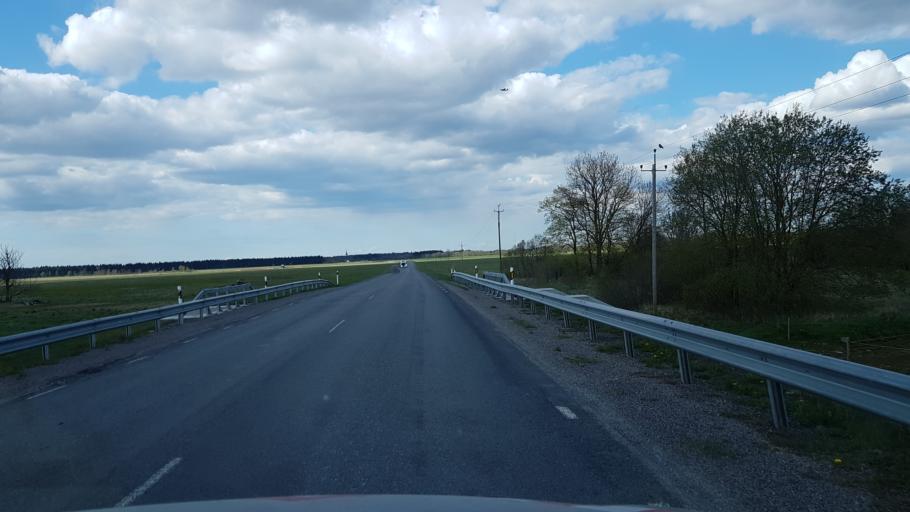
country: EE
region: Harju
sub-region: Keila linn
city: Keila
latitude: 59.2775
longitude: 24.4514
